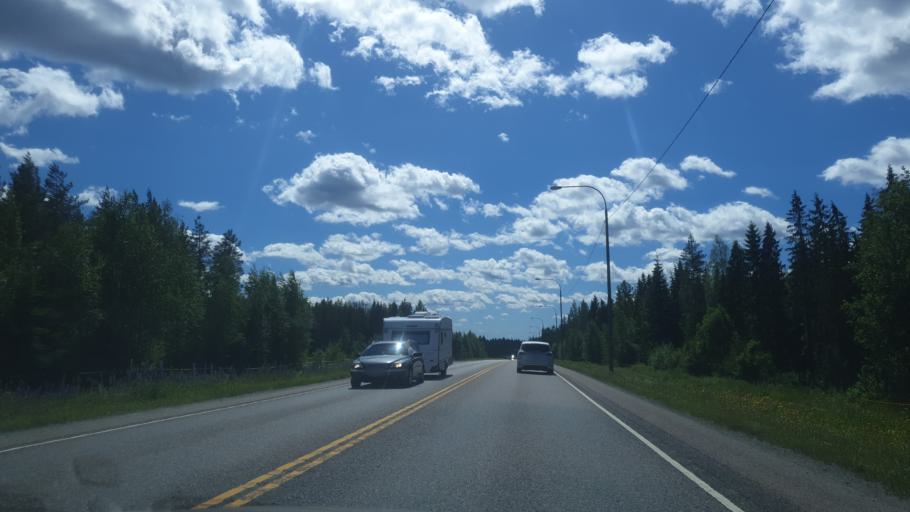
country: FI
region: Northern Savo
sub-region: Varkaus
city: Varkaus
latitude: 62.3691
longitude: 27.8097
